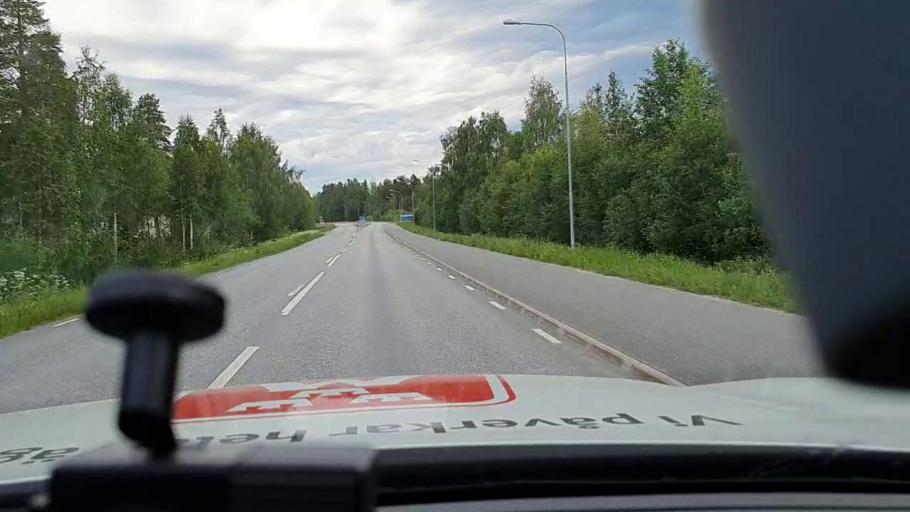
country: SE
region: Norrbotten
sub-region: Bodens Kommun
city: Boden
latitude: 65.8124
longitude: 21.6503
